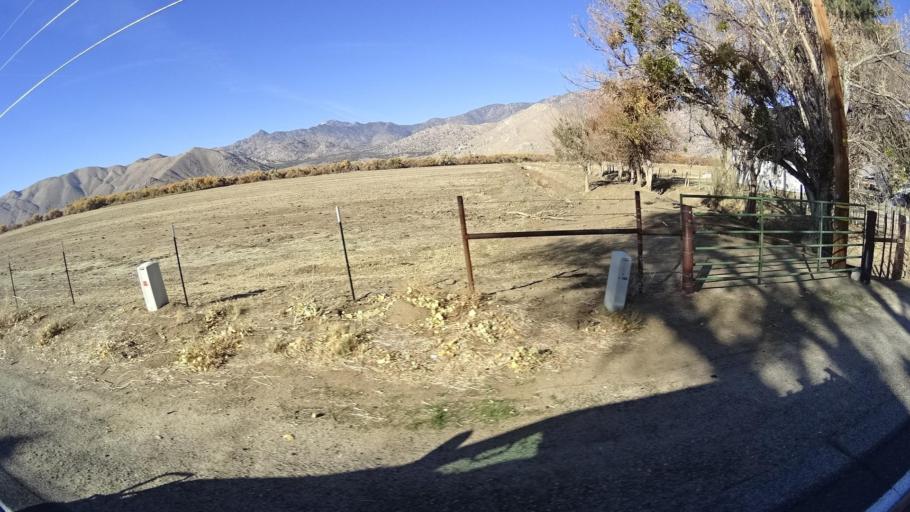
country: US
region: California
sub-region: Kern County
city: Weldon
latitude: 35.6667
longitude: -118.2812
